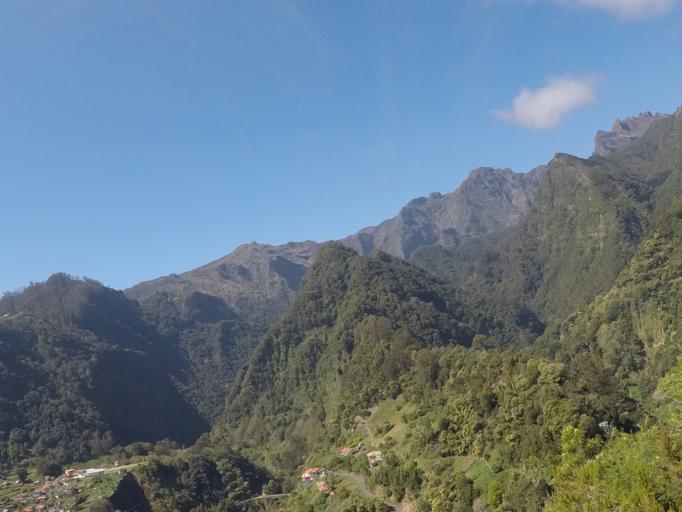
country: PT
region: Madeira
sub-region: Santana
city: Santana
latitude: 32.7600
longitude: -16.8762
